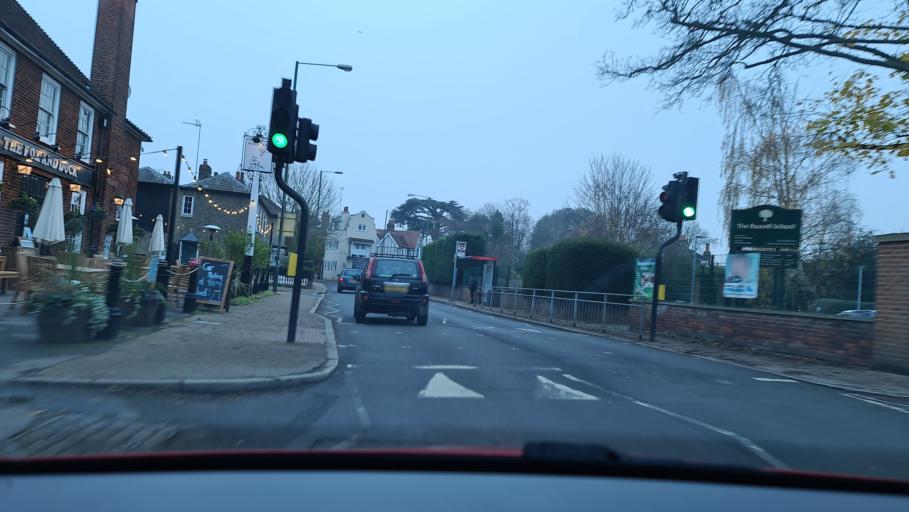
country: GB
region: England
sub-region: Greater London
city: Richmond
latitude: 51.4451
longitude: -0.3030
